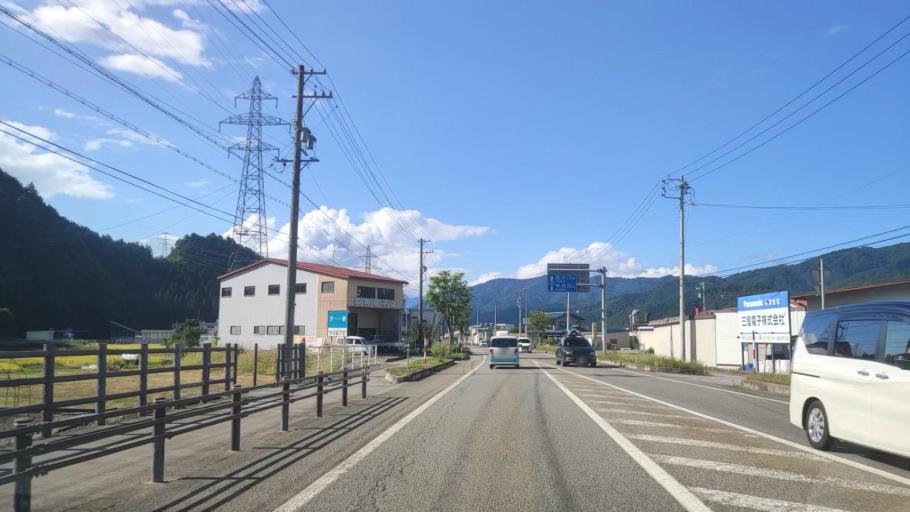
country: JP
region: Gifu
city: Takayama
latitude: 36.2354
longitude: 137.1778
